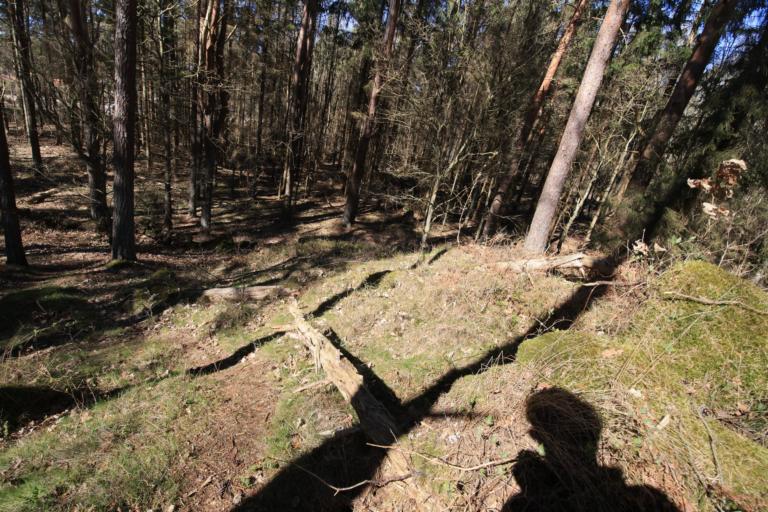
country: SE
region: Halland
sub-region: Varbergs Kommun
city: Varberg
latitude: 57.1821
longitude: 12.2304
